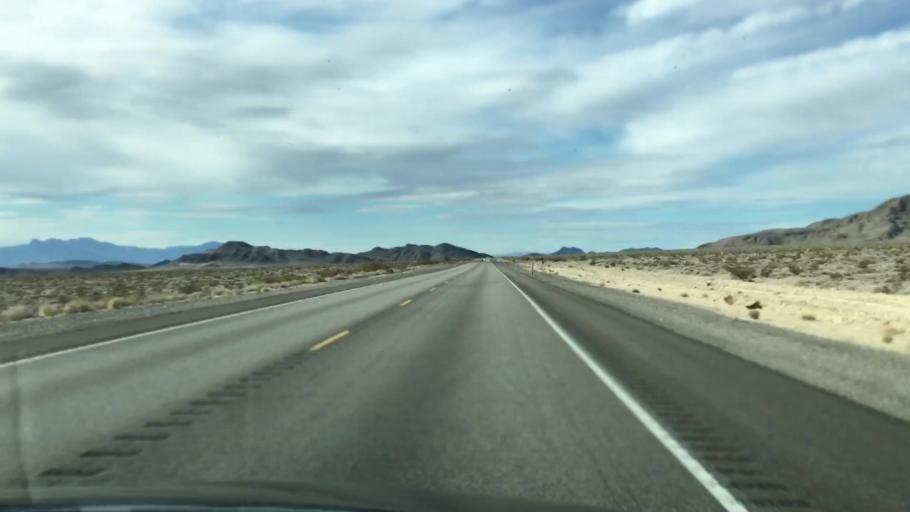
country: US
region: Nevada
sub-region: Nye County
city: Pahrump
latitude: 36.5712
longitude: -116.1682
